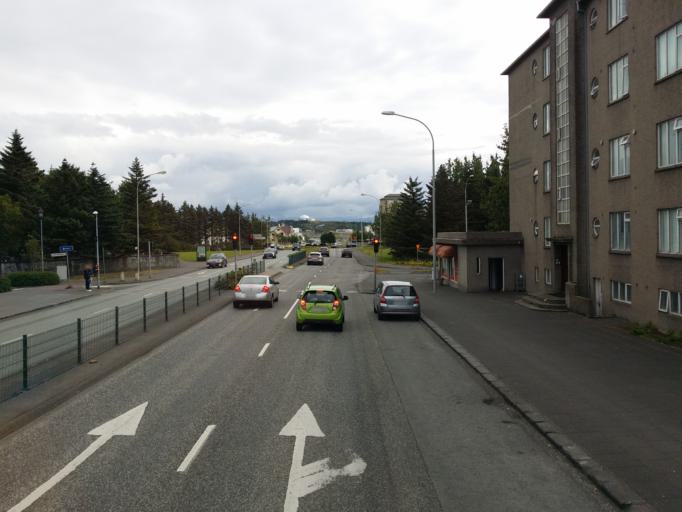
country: IS
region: Capital Region
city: Seltjarnarnes
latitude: 64.1443
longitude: -21.9513
